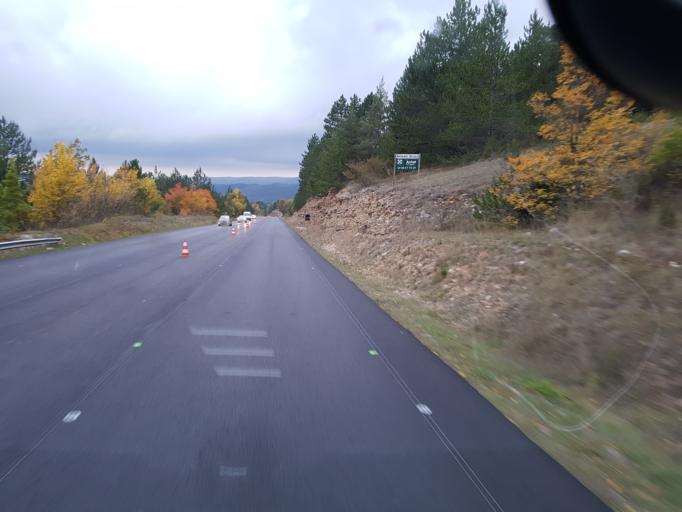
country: FR
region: Languedoc-Roussillon
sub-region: Departement de la Lozere
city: Mende
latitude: 44.5352
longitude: 3.6005
